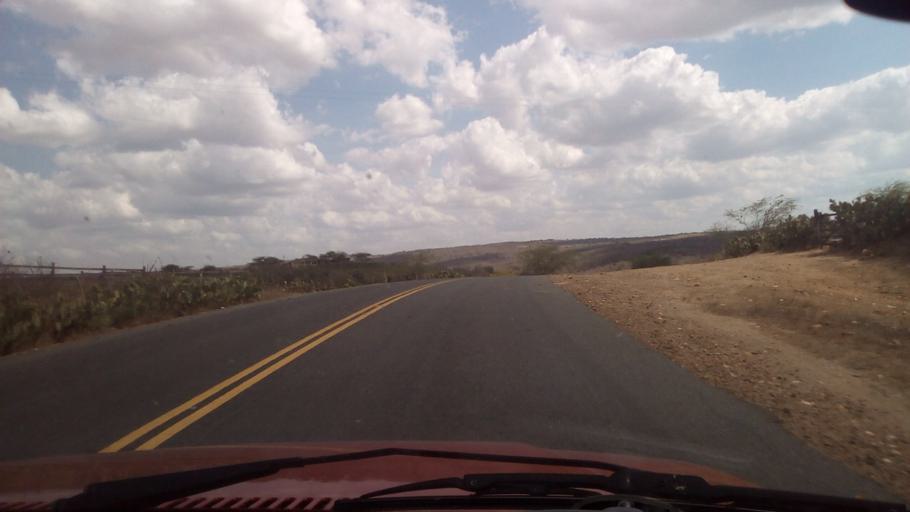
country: BR
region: Paraiba
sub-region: Bananeiras
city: Bananeiras
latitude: -6.7129
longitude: -35.7213
